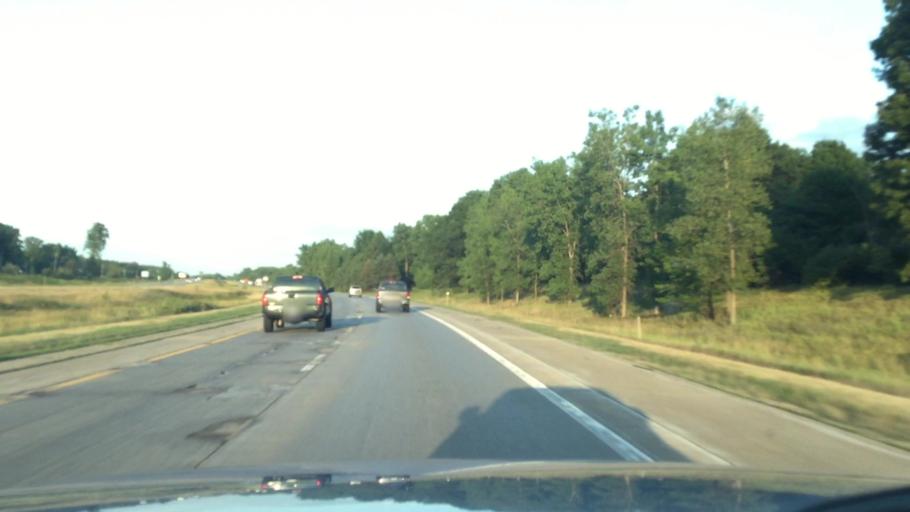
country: US
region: Michigan
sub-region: Ingham County
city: Haslett
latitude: 42.7961
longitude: -84.3643
